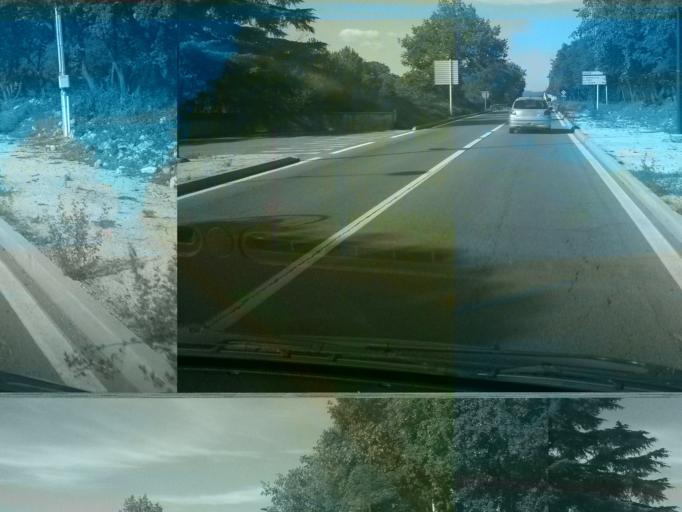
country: FR
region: Languedoc-Roussillon
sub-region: Departement du Gard
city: Quissac
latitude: 43.9175
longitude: 3.9931
